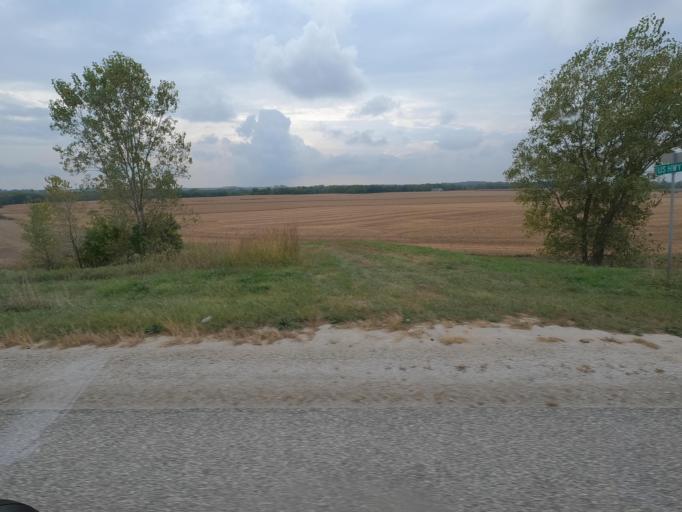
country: US
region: Iowa
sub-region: Wapello County
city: Eddyville
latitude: 41.1255
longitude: -92.5633
